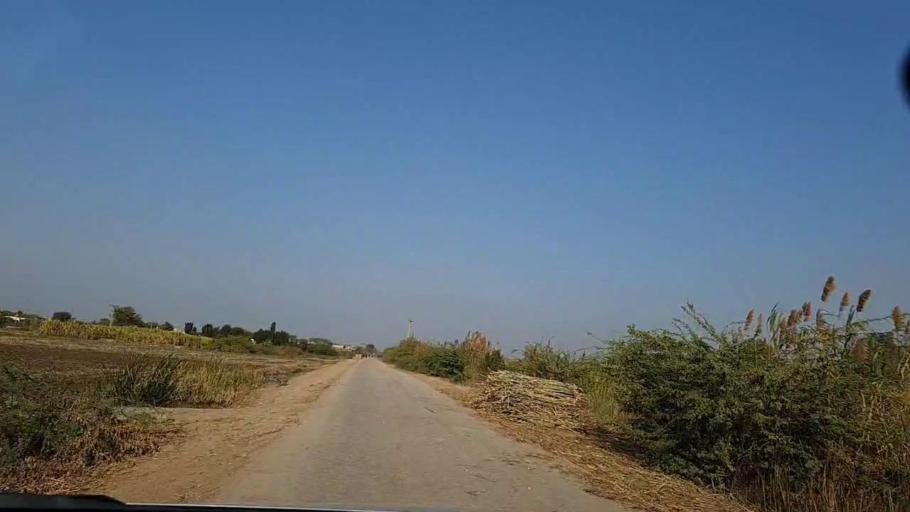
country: PK
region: Sindh
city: Mirwah Gorchani
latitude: 25.2369
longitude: 68.9851
